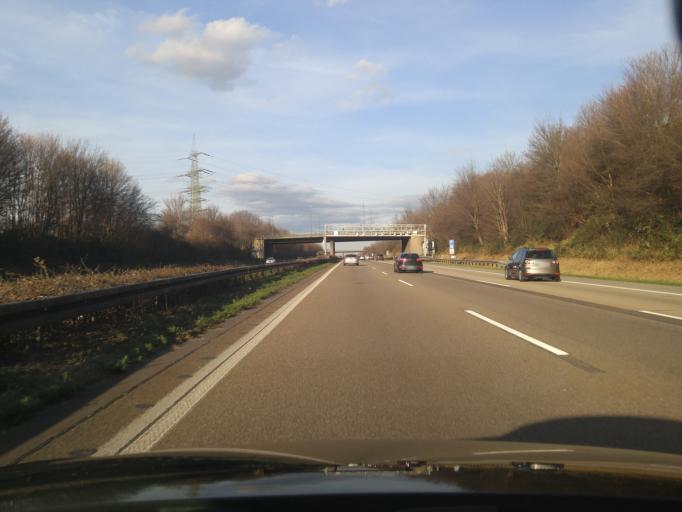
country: DE
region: North Rhine-Westphalia
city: Opladen
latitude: 51.0759
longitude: 6.9882
